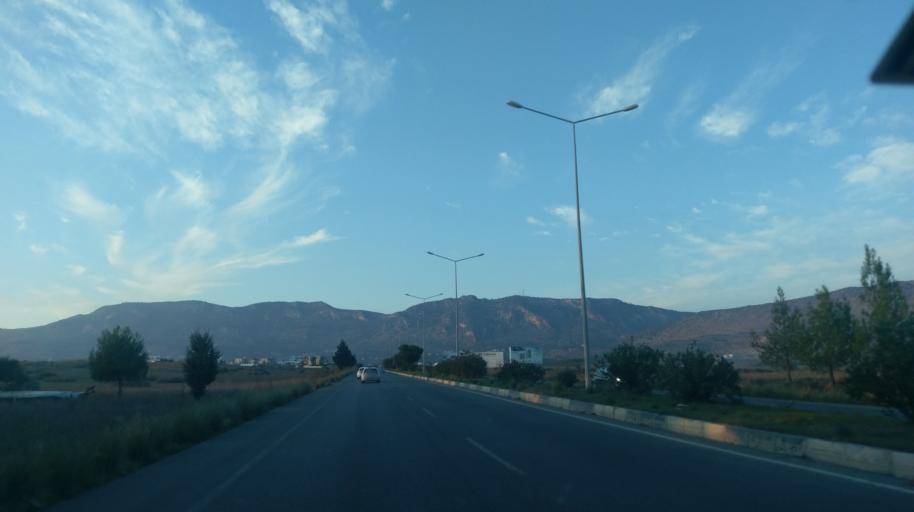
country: CY
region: Keryneia
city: Kyrenia
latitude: 35.2642
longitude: 33.2942
